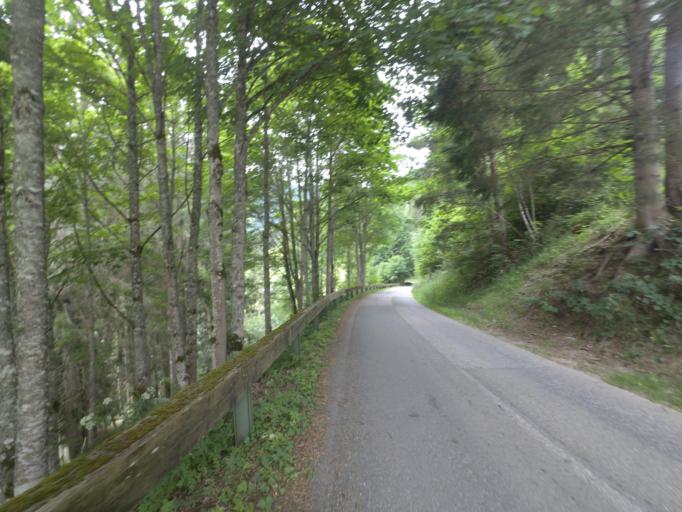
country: AT
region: Salzburg
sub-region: Politischer Bezirk Zell am See
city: Leogang
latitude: 47.4307
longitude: 12.7476
